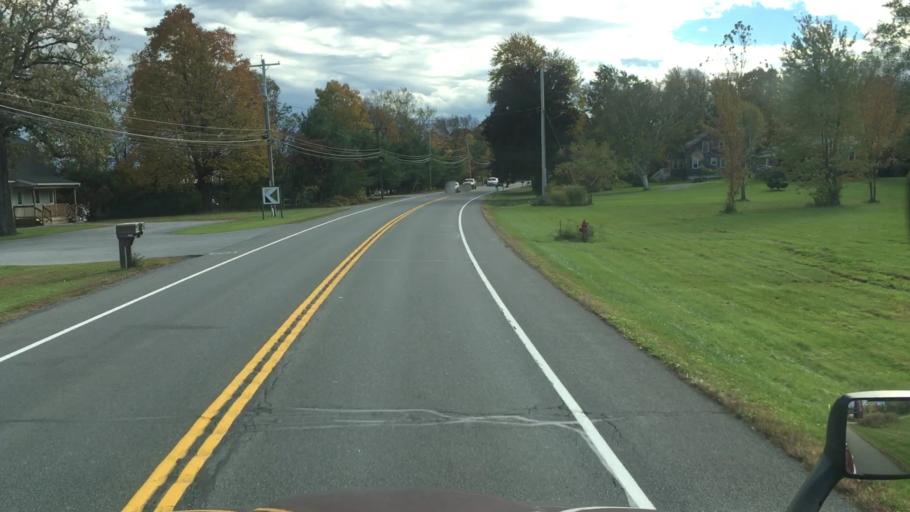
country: US
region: New York
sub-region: Saratoga County
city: Ballston Spa
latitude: 42.9642
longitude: -73.8633
